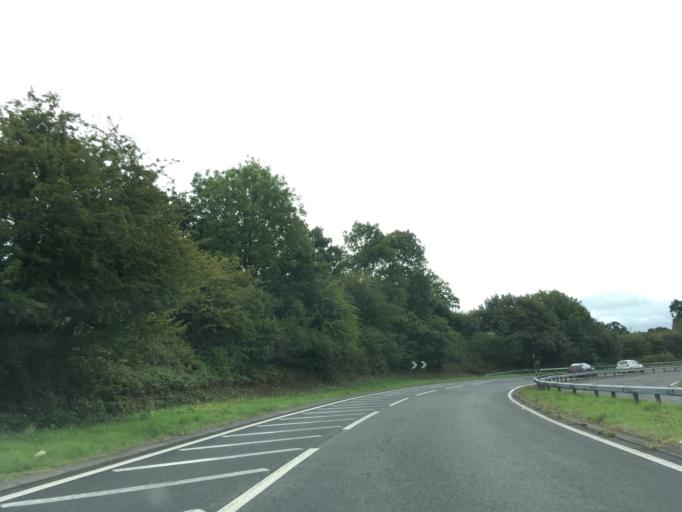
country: GB
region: Wales
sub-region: Monmouthshire
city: Llanarth
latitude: 51.7681
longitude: -2.8317
